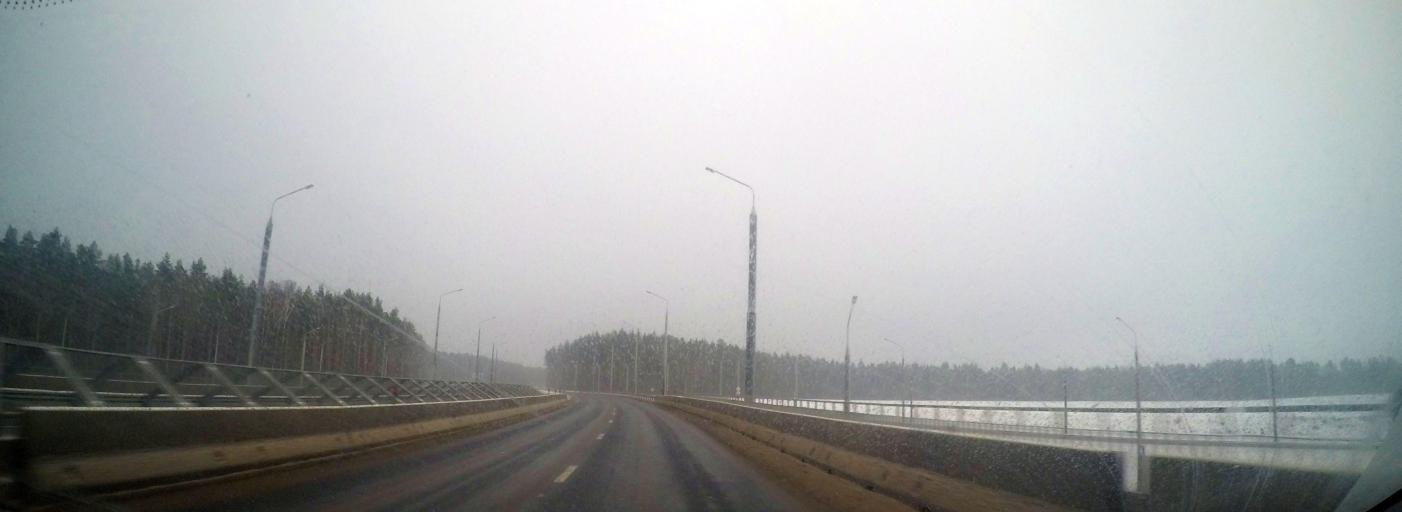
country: BY
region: Grodnenskaya
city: Hrodna
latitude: 53.6377
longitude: 23.8808
